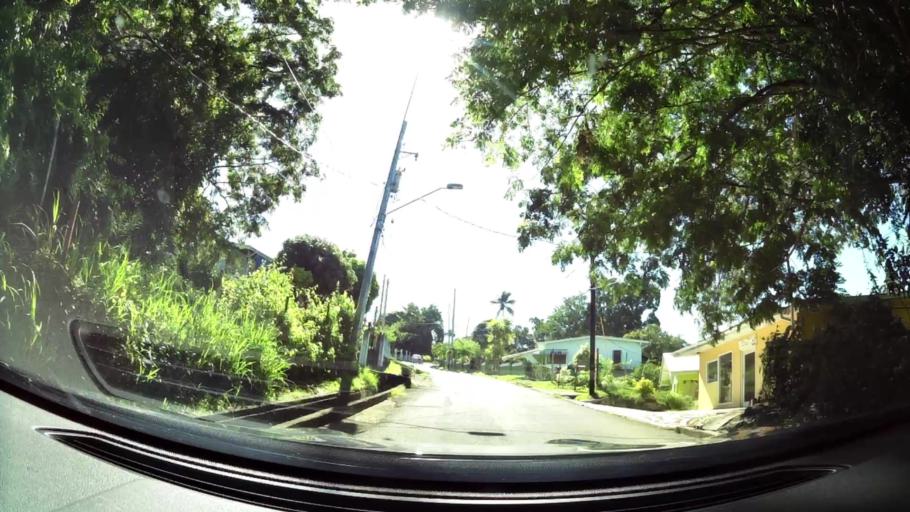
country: TT
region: Tobago
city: Scarborough
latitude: 11.1807
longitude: -60.7292
